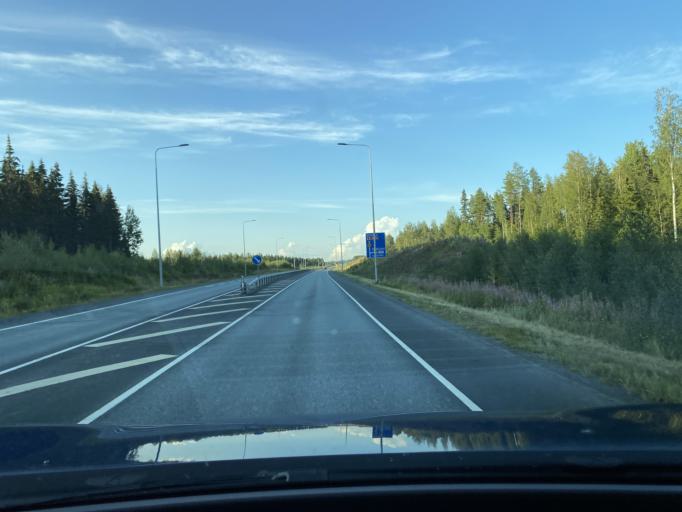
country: FI
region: Southern Ostrobothnia
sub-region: Seinaejoki
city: Seinaejoki
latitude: 62.6856
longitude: 22.8022
